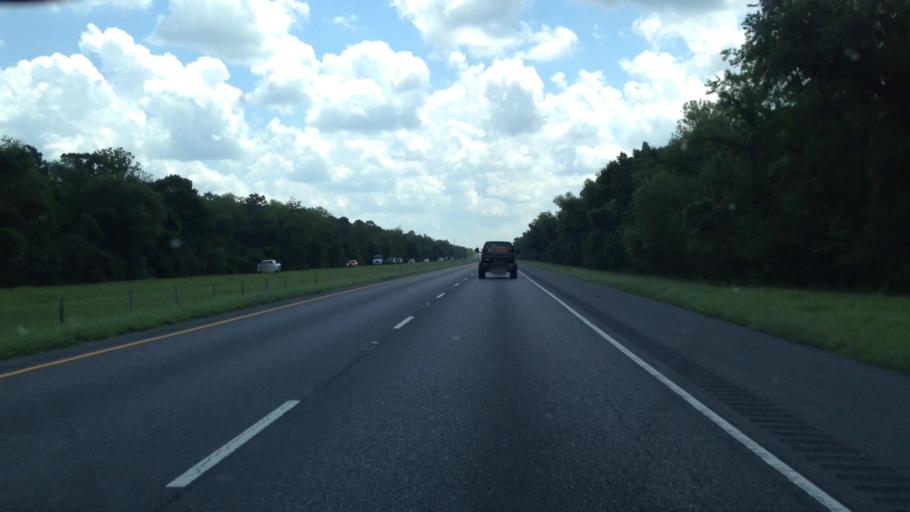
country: US
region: Louisiana
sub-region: Saint James Parish
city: Grand Point
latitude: 30.1356
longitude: -90.7331
